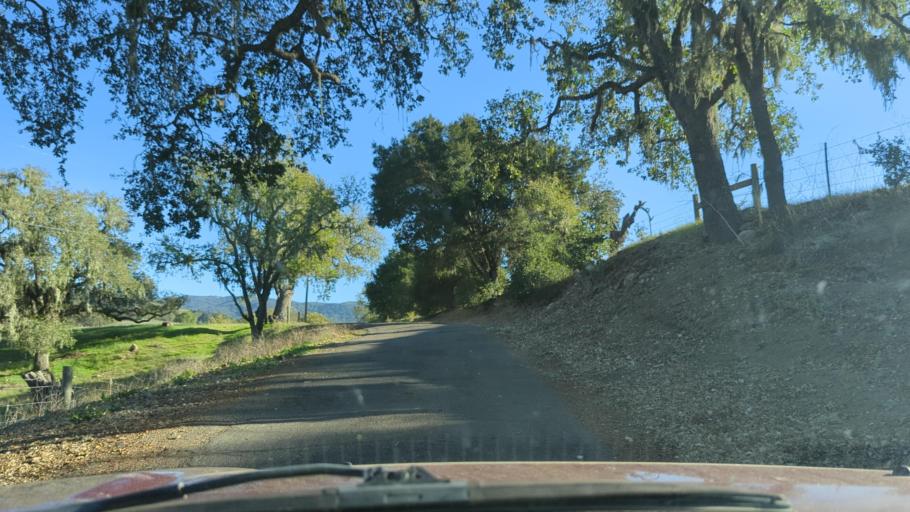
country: US
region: California
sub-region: Santa Barbara County
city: Santa Ynez
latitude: 34.5724
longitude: -120.0975
